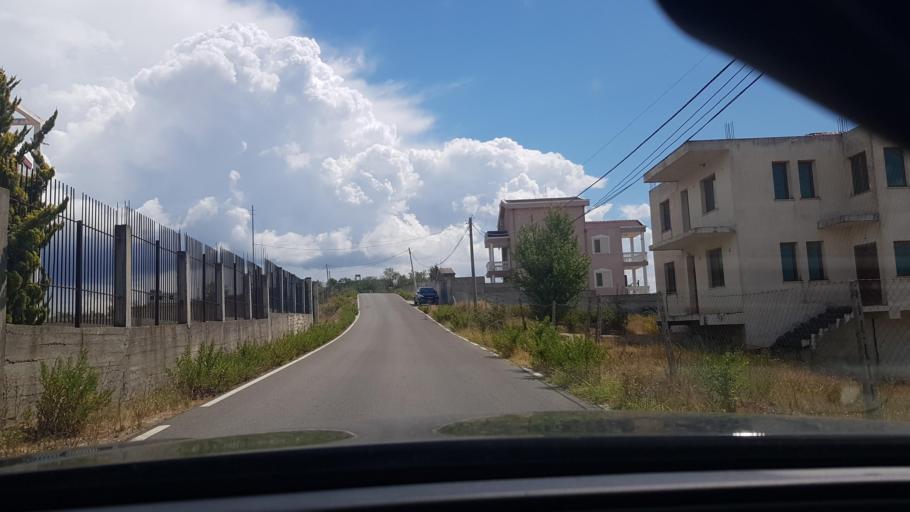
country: AL
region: Durres
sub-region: Rrethi i Durresit
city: Rrashbull
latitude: 41.2931
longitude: 19.5350
